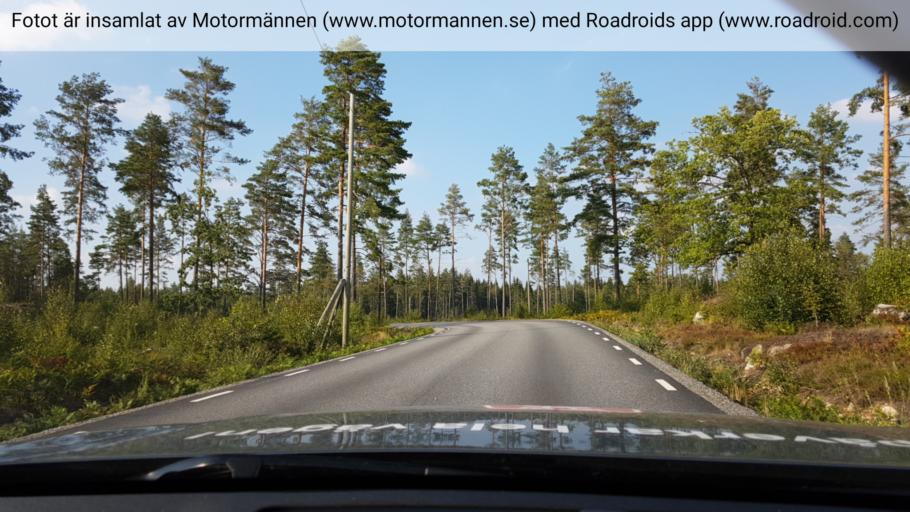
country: SE
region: Soedermanland
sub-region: Strangnas Kommun
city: Mariefred
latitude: 59.1517
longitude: 17.2010
